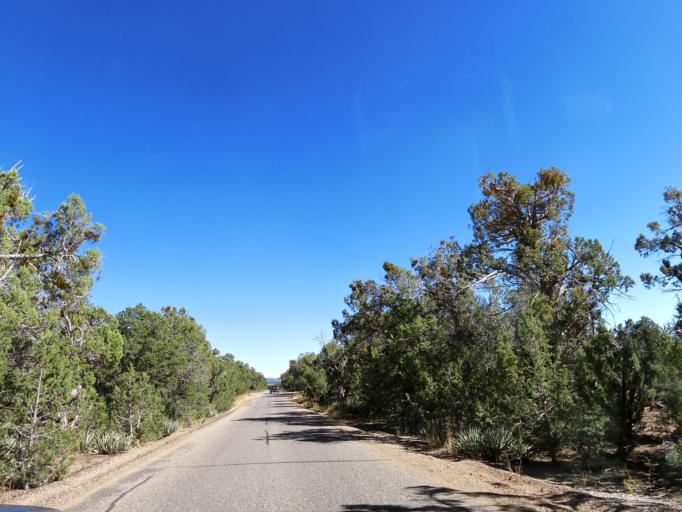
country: US
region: Colorado
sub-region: Montezuma County
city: Cortez
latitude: 37.1652
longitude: -108.4866
